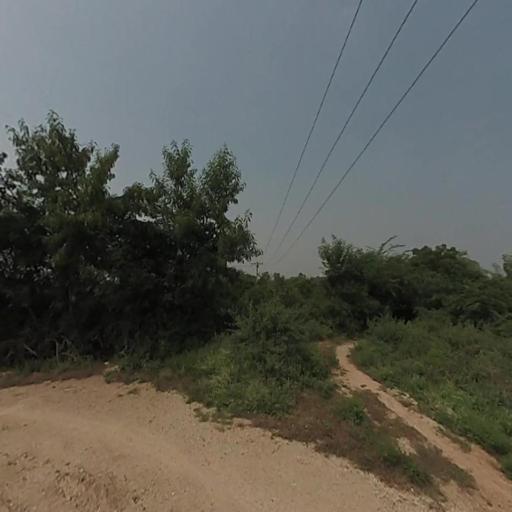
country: IN
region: Telangana
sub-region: Nalgonda
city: Nalgonda
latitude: 17.2076
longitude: 79.1569
